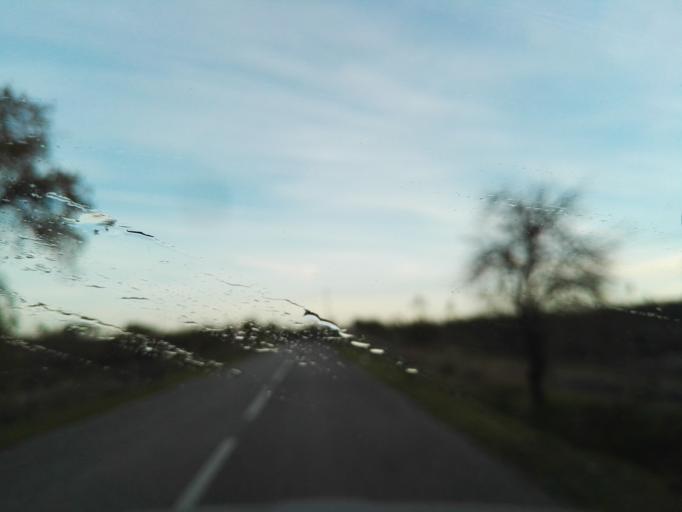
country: PT
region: Evora
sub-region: Montemor-O-Novo
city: Montemor-o-Novo
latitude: 38.7830
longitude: -8.2189
